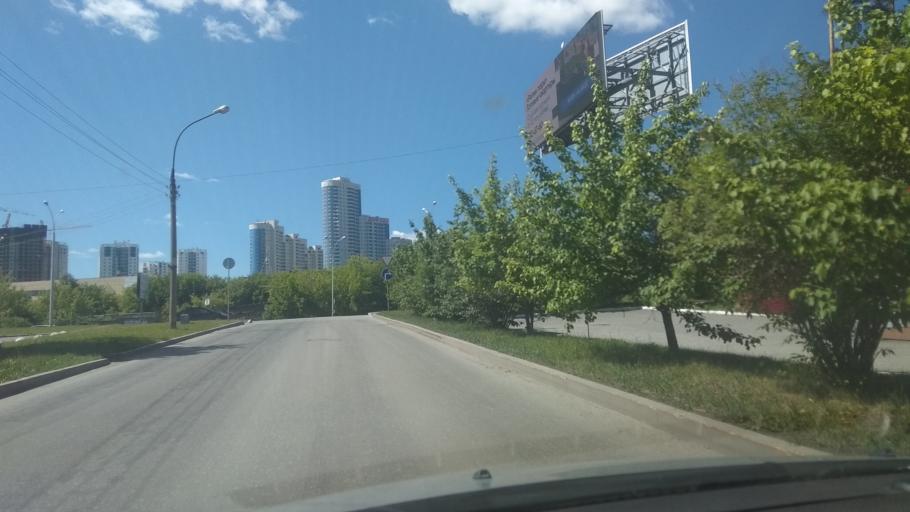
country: RU
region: Sverdlovsk
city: Yekaterinburg
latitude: 56.8225
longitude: 60.5623
